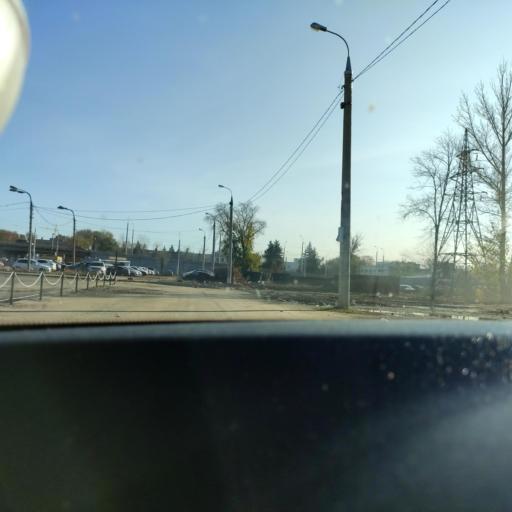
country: RU
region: Samara
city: Smyshlyayevka
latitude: 53.2080
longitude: 50.2739
